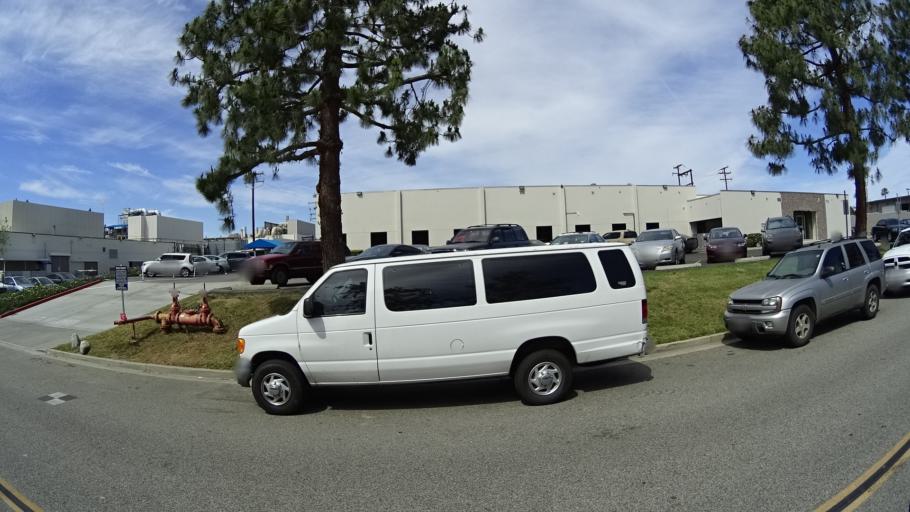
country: US
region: California
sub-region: Ventura County
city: Casa Conejo
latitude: 34.1877
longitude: -118.9269
